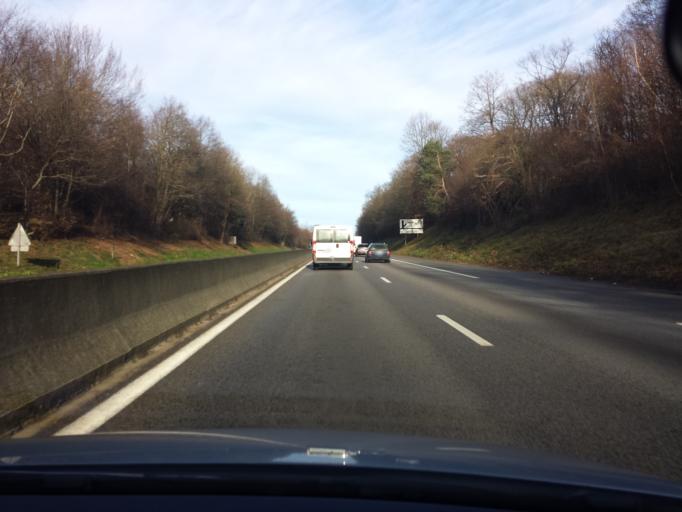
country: FR
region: Ile-de-France
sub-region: Departement des Yvelines
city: Chambourcy
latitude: 48.8957
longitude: 2.0070
